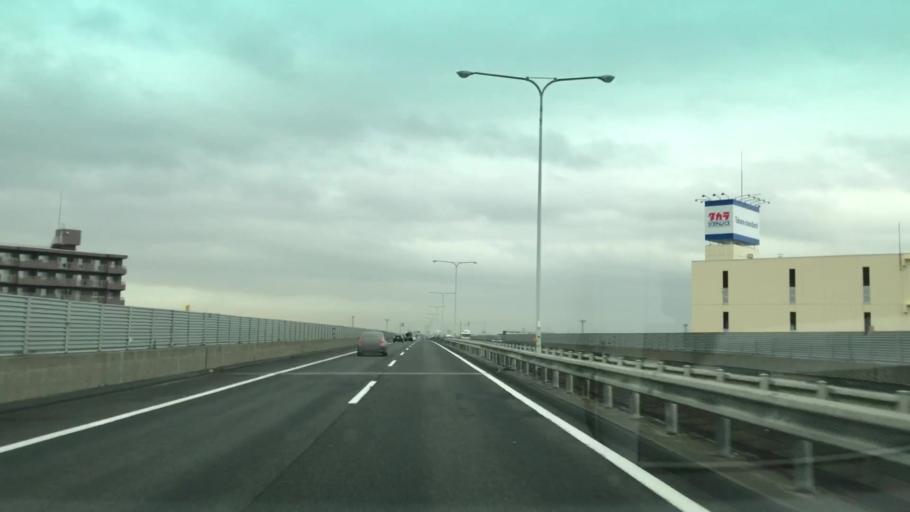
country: JP
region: Hokkaido
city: Sapporo
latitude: 43.0379
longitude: 141.4403
